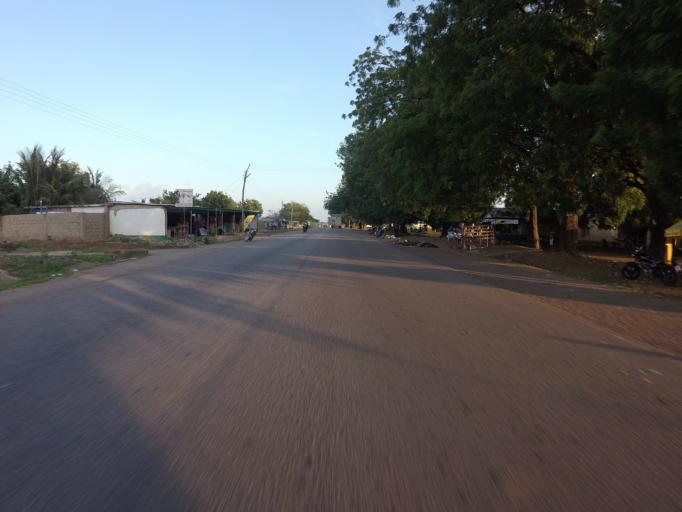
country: GH
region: Upper East
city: Navrongo
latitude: 10.9684
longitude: -1.1019
